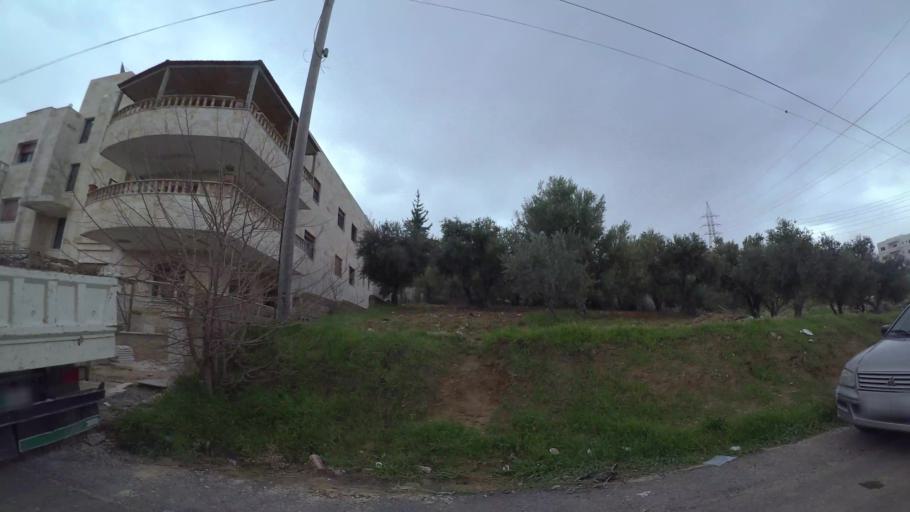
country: JO
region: Amman
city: Umm as Summaq
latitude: 31.9091
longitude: 35.8341
